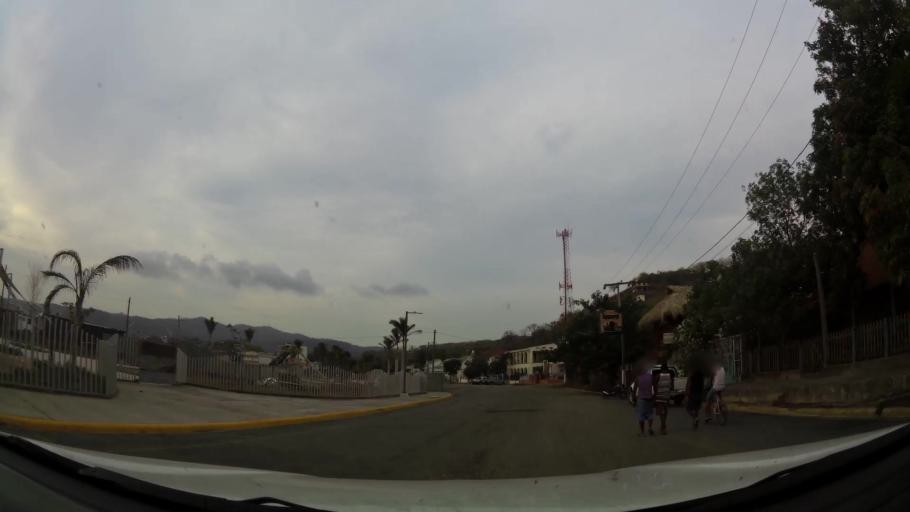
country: NI
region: Rivas
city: San Juan del Sur
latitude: 11.2498
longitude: -85.8742
